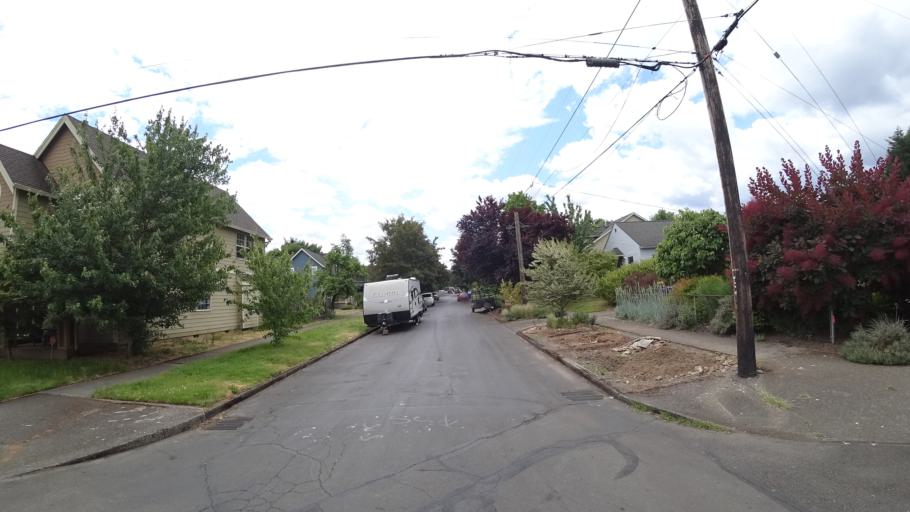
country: US
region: Oregon
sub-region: Multnomah County
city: Portland
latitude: 45.5853
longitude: -122.7174
